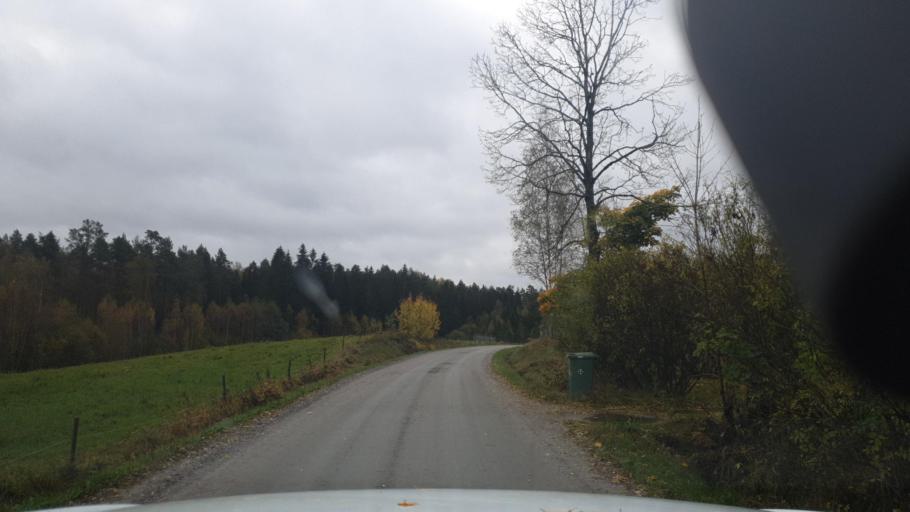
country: SE
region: Vaermland
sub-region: Karlstads Kommun
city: Edsvalla
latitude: 59.5035
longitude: 13.0304
